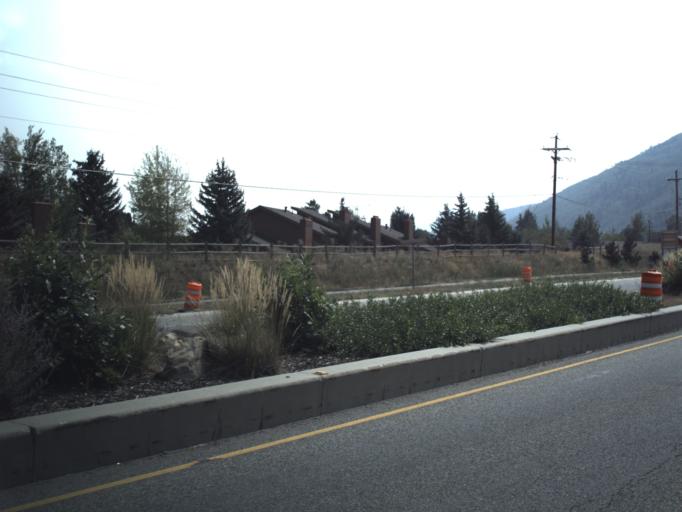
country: US
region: Utah
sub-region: Summit County
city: Snyderville
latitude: 40.6890
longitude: -111.5443
